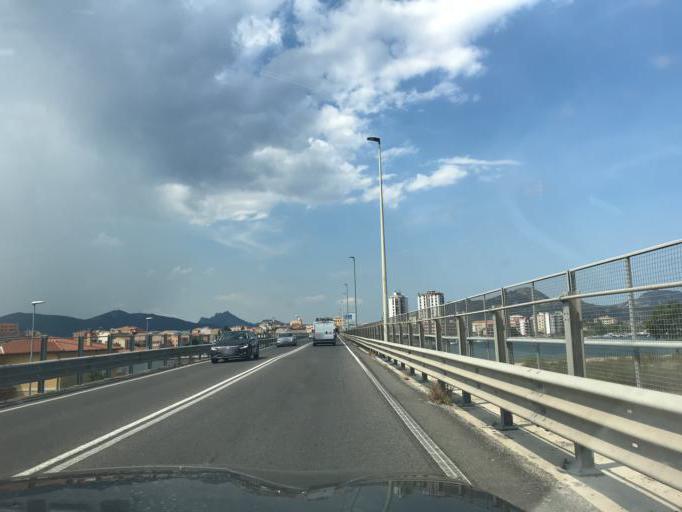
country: IT
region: Sardinia
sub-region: Provincia di Olbia-Tempio
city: Olbia
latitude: 40.9163
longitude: 9.5017
